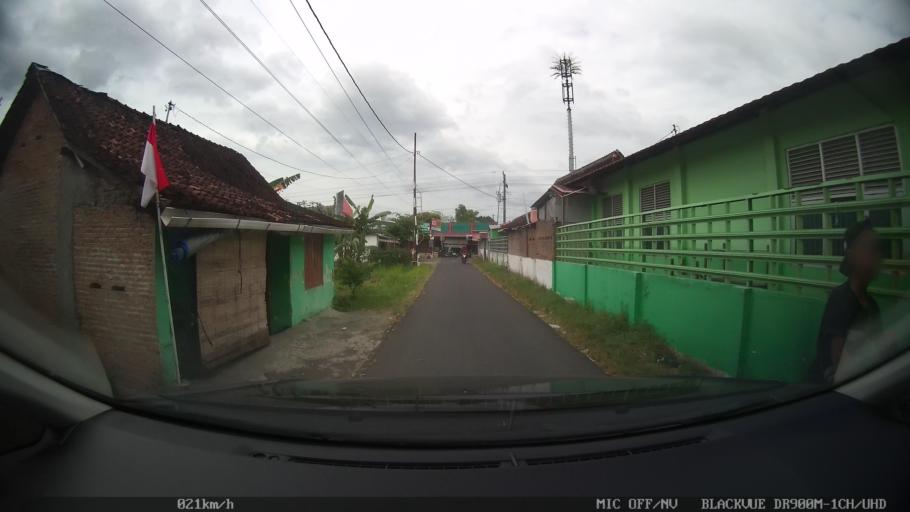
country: ID
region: Daerah Istimewa Yogyakarta
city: Depok
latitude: -7.8196
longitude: 110.4203
